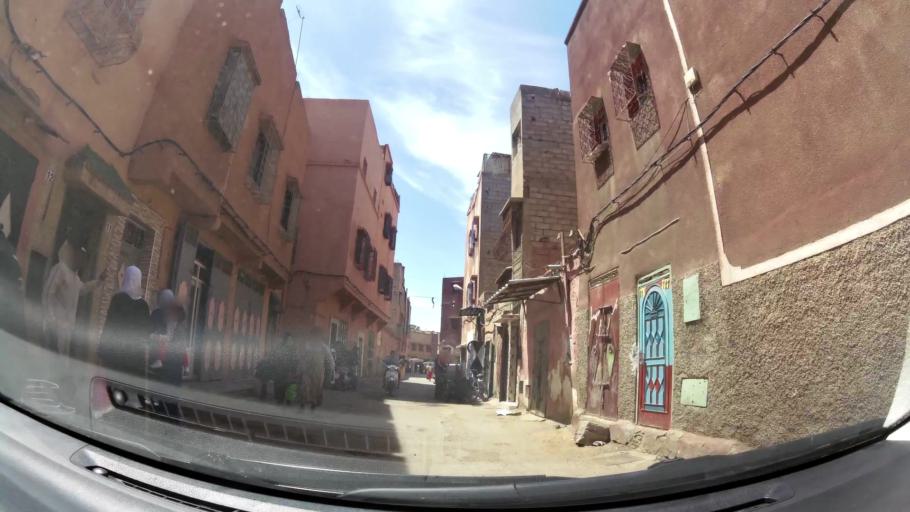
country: MA
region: Marrakech-Tensift-Al Haouz
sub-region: Marrakech
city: Marrakesh
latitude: 31.6172
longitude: -7.9665
